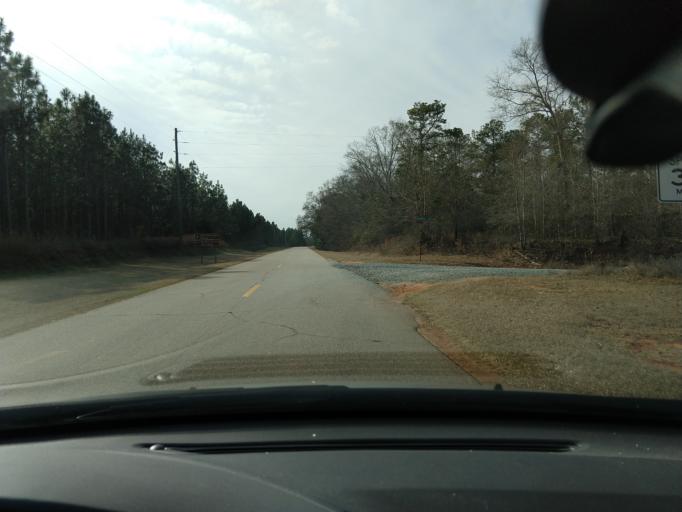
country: US
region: Georgia
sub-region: Webster County
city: Preston
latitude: 32.0261
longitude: -84.4280
